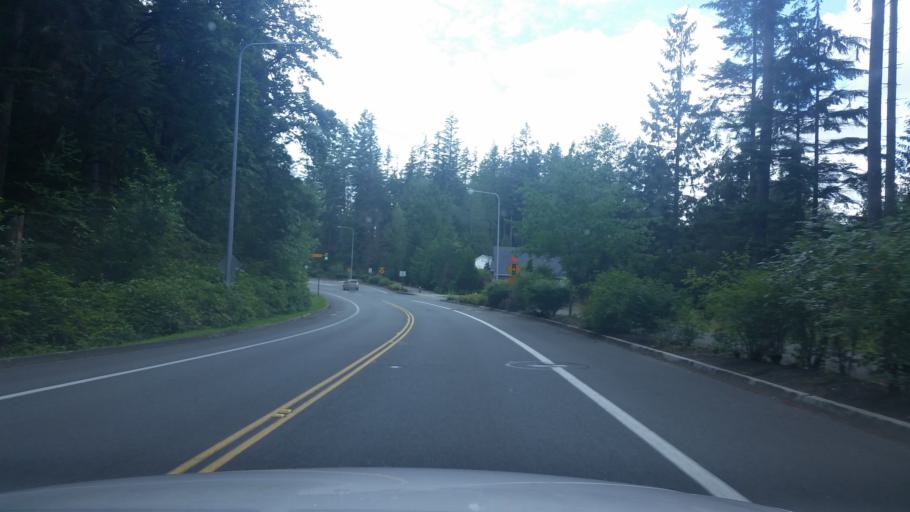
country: US
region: Washington
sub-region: King County
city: Union Hill-Novelty Hill
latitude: 47.7154
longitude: -122.0268
